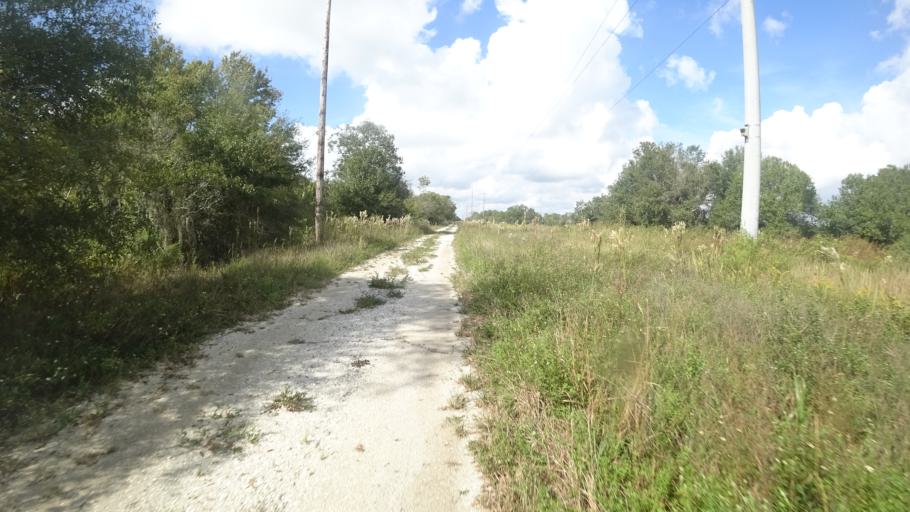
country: US
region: Florida
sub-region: Hillsborough County
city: Wimauma
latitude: 27.5158
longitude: -82.1134
